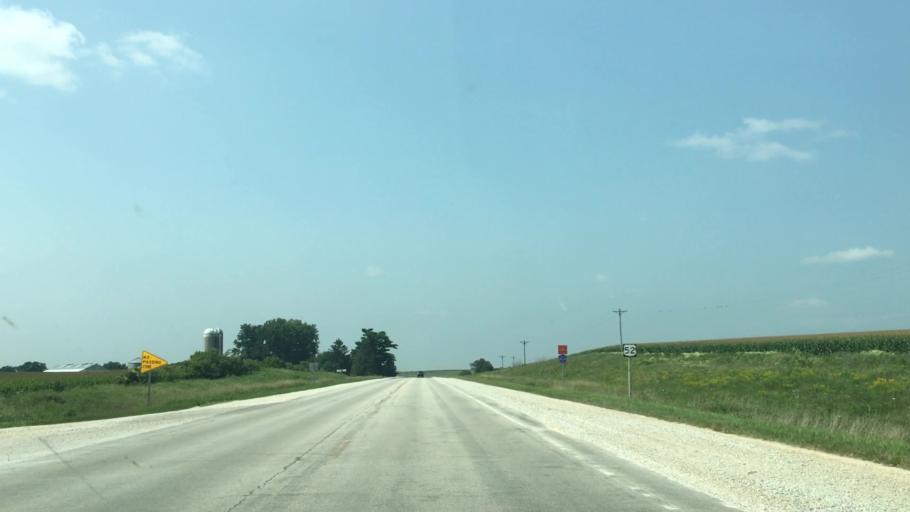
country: US
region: Iowa
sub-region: Winneshiek County
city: Decorah
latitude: 43.4107
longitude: -91.8569
